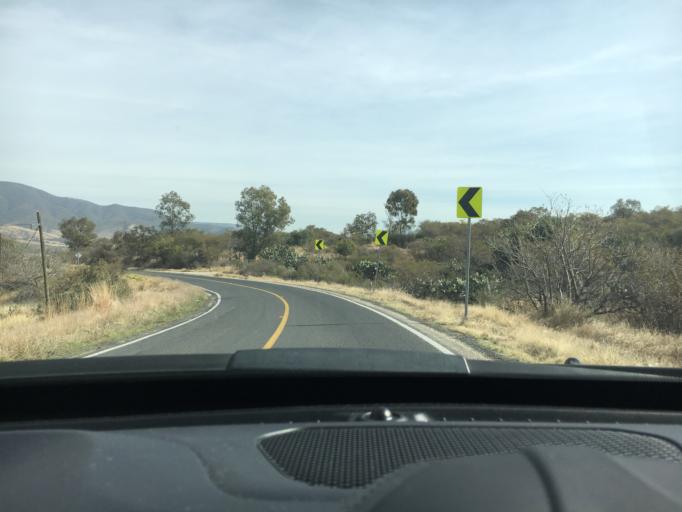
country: MX
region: Guanajuato
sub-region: Silao de la Victoria
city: San Francisco (Banos de Agua Caliente)
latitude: 21.0677
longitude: -101.4971
